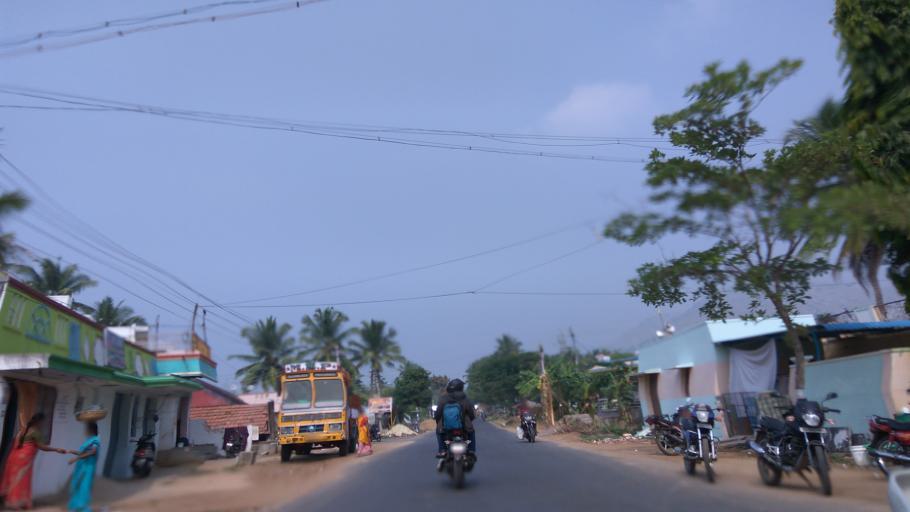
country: IN
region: Tamil Nadu
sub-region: Krishnagiri
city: Kaverippattanam
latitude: 12.4639
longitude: 78.2093
